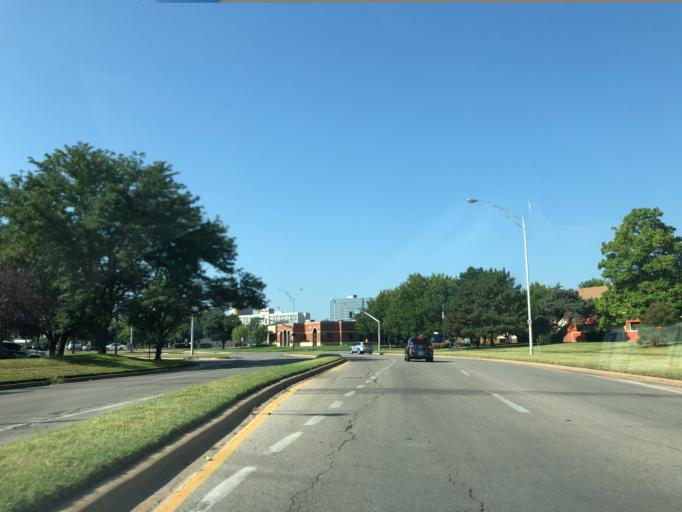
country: US
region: Kansas
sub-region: Sedgwick County
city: Wichita
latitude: 37.6944
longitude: -97.3417
